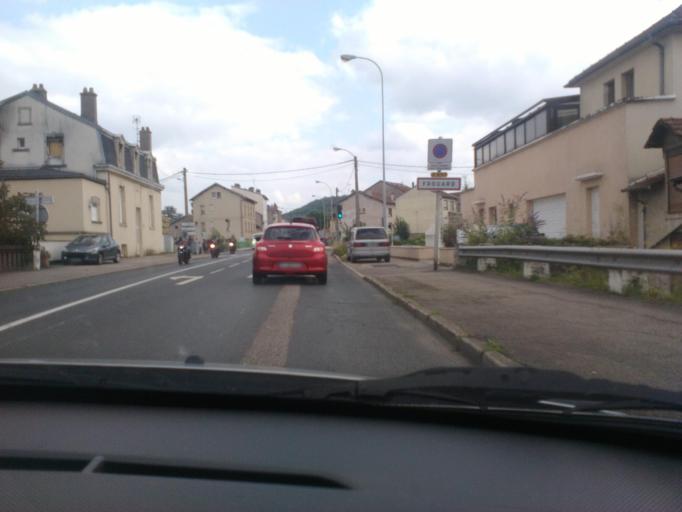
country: FR
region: Lorraine
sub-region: Departement de Meurthe-et-Moselle
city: Frouard
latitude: 48.7622
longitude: 6.1313
